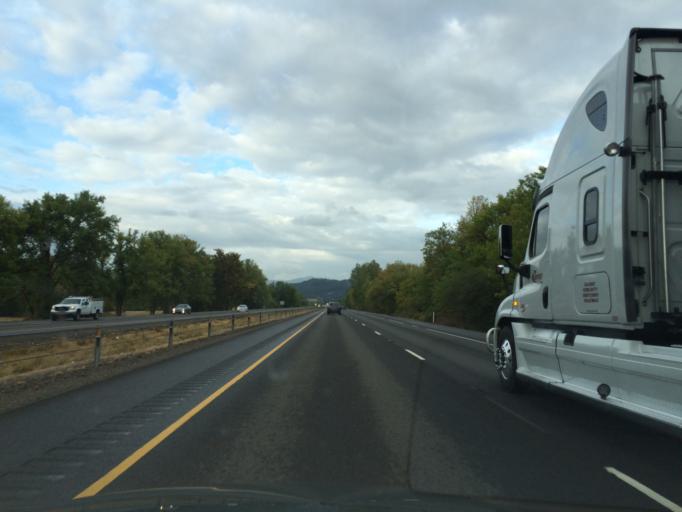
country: US
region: Oregon
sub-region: Lane County
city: Cottage Grove
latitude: 43.7536
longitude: -123.1032
